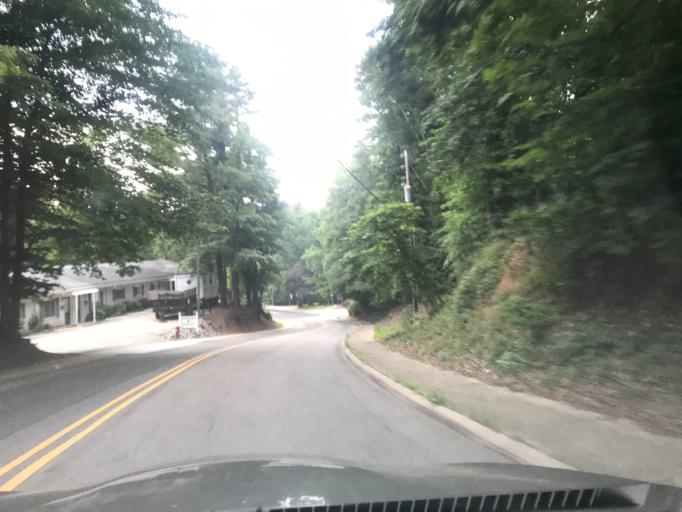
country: US
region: North Carolina
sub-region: Orange County
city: Chapel Hill
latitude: 35.9218
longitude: -79.0517
